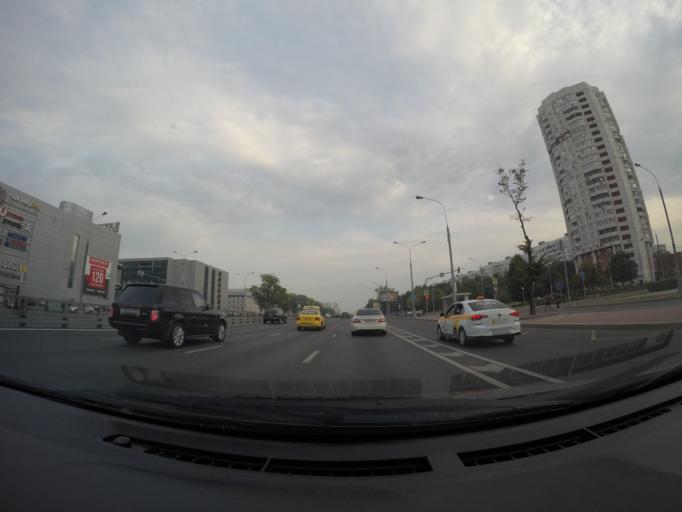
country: RU
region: Moscow
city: Orekhovo-Borisovo
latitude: 55.6159
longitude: 37.7148
